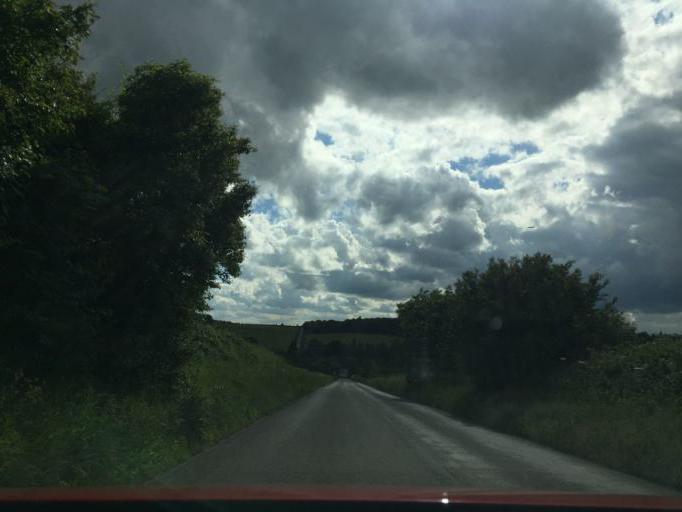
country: GB
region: England
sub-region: Hertfordshire
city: Harpenden
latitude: 51.8524
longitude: -0.3664
